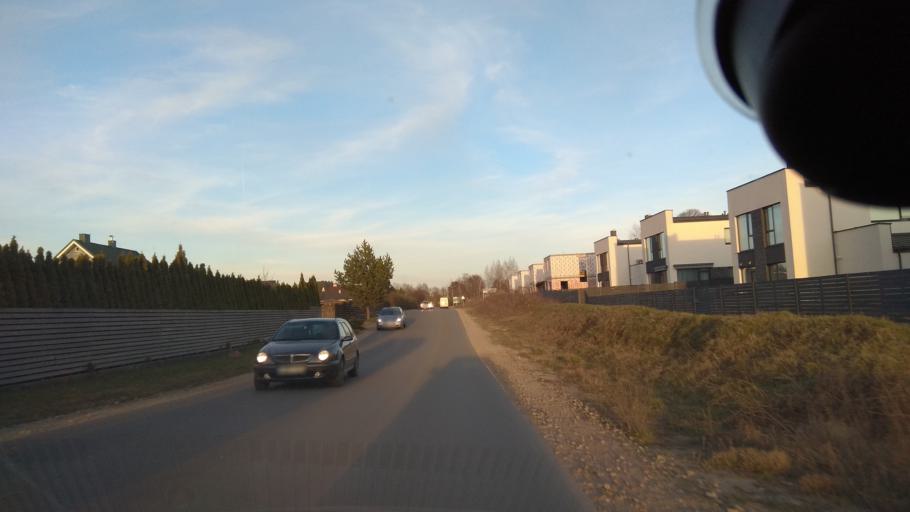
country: LT
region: Vilnius County
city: Pasilaiciai
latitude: 54.7578
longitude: 25.2258
